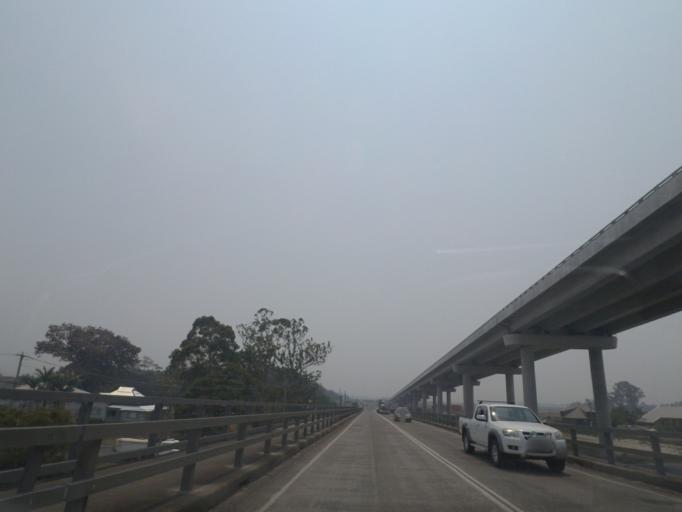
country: AU
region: New South Wales
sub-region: Clarence Valley
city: Maclean
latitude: -29.4278
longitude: 153.2410
